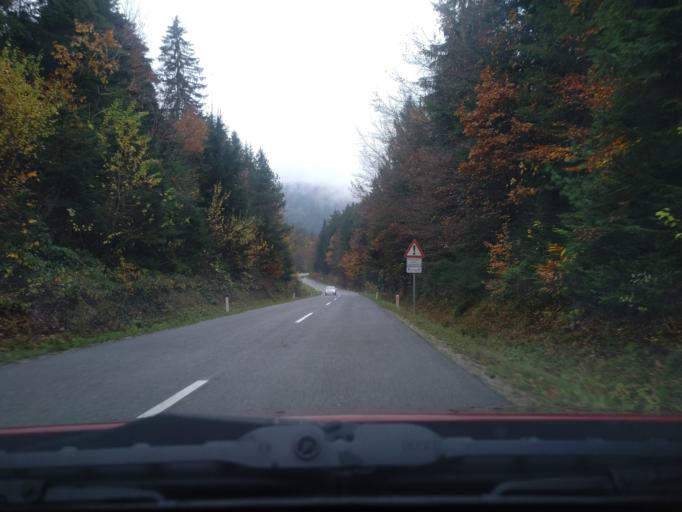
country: SI
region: Ljubno
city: Ljubno ob Savinji
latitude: 46.3227
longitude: 14.8489
